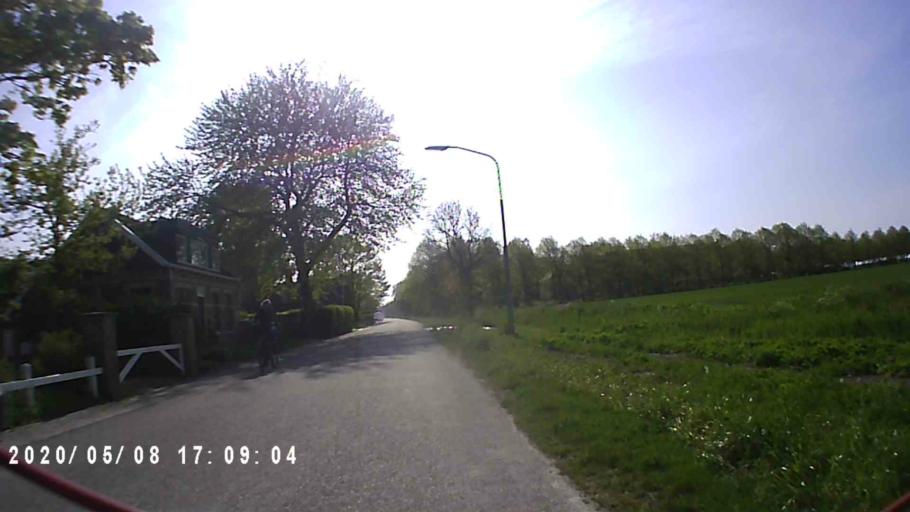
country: NL
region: Groningen
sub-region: Gemeente Winsum
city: Winsum
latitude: 53.4017
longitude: 6.5894
